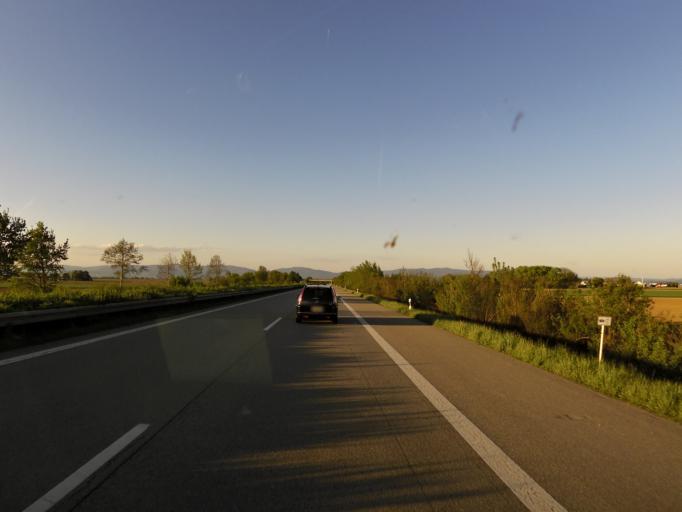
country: DE
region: Bavaria
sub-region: Lower Bavaria
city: Otzing
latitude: 48.7632
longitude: 12.7736
